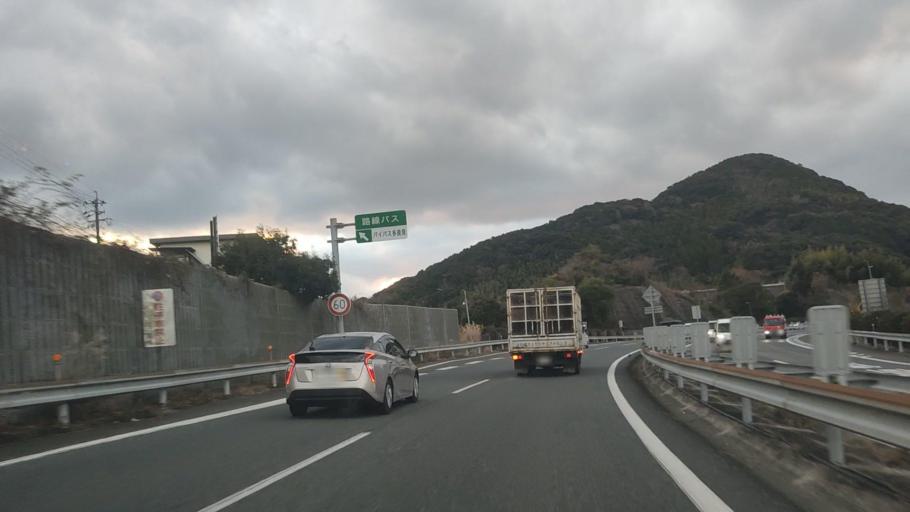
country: JP
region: Nagasaki
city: Obita
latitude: 32.8118
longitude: 129.9607
